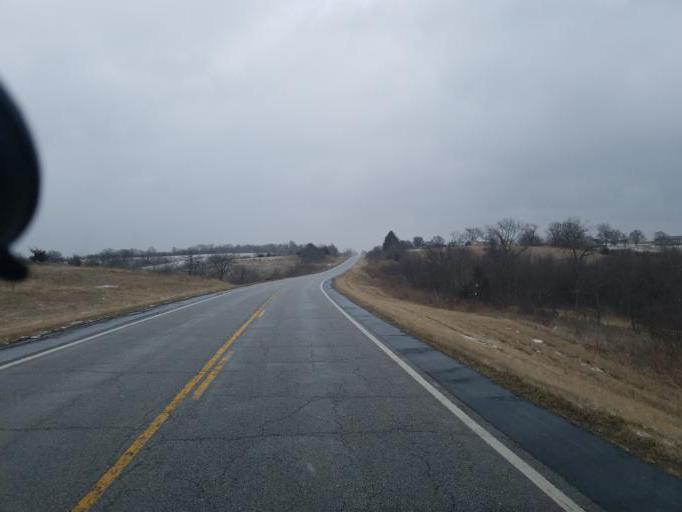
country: US
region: Missouri
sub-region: Putnam County
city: Unionville
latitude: 40.4717
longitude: -92.9358
